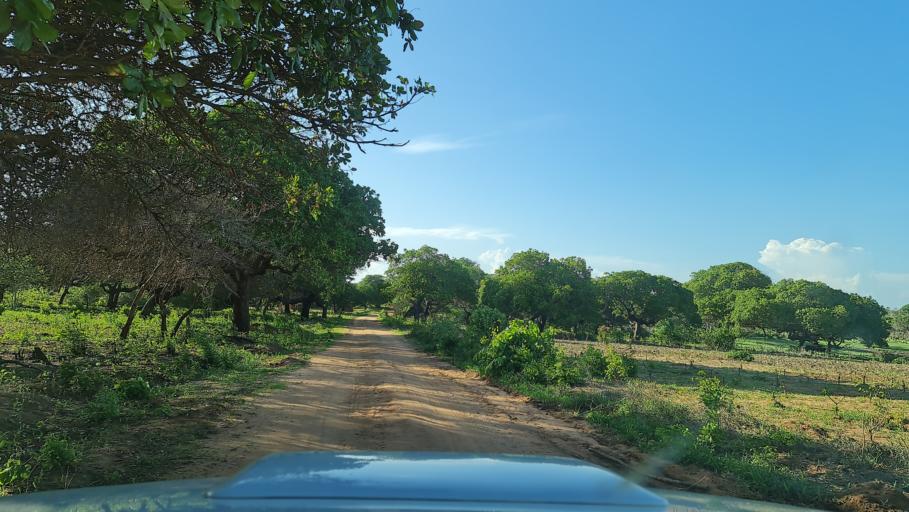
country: MZ
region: Nampula
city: Nacala
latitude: -14.7116
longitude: 40.3363
